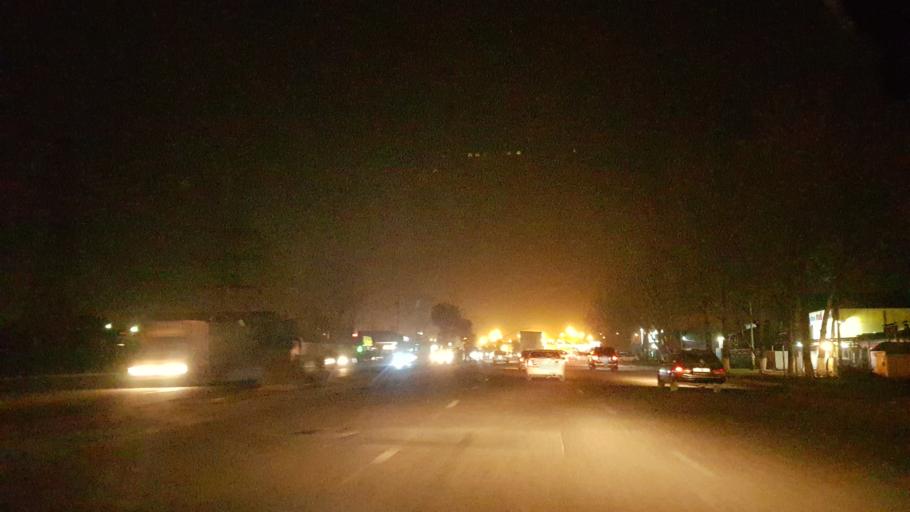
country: KZ
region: Almaty Qalasy
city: Almaty
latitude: 43.2588
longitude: 76.8476
